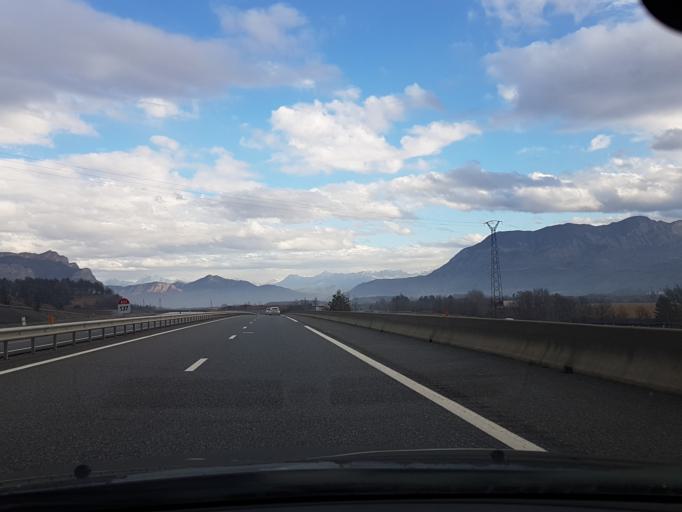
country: FR
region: Provence-Alpes-Cote d'Azur
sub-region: Departement des Hautes-Alpes
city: Laragne-Monteglin
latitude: 44.3398
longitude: 5.9018
